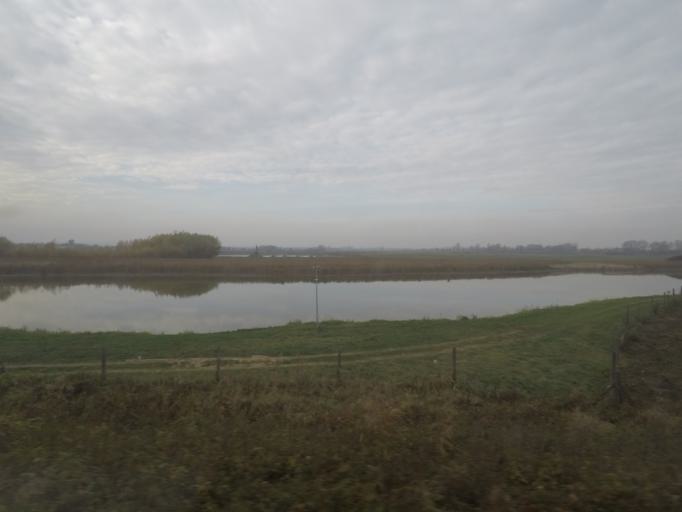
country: PL
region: Subcarpathian Voivodeship
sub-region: Powiat przemyski
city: Medyka
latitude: 49.7869
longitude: 22.8754
